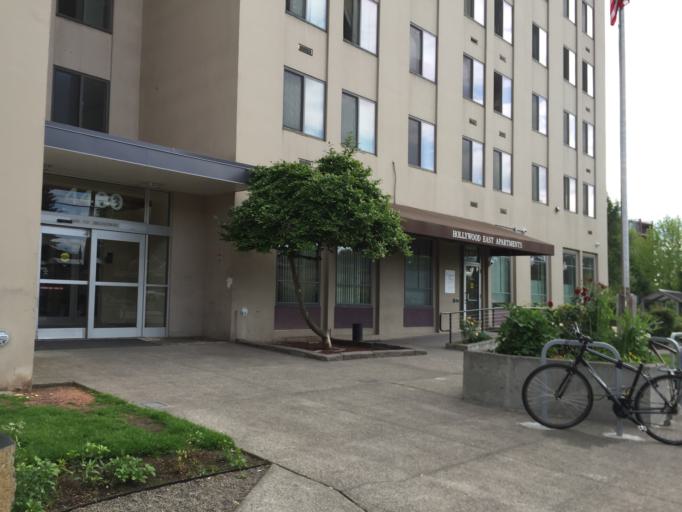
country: US
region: Oregon
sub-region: Multnomah County
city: Portland
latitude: 45.5351
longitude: -122.6176
